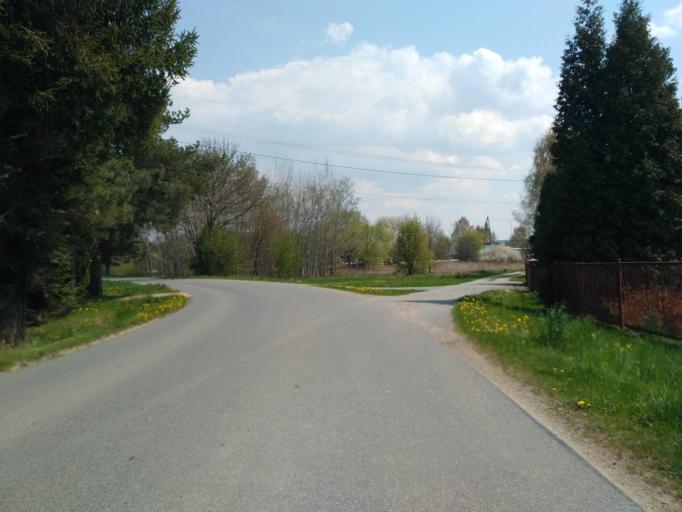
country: PL
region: Subcarpathian Voivodeship
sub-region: Powiat jasielski
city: Tarnowiec
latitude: 49.7454
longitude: 21.5565
